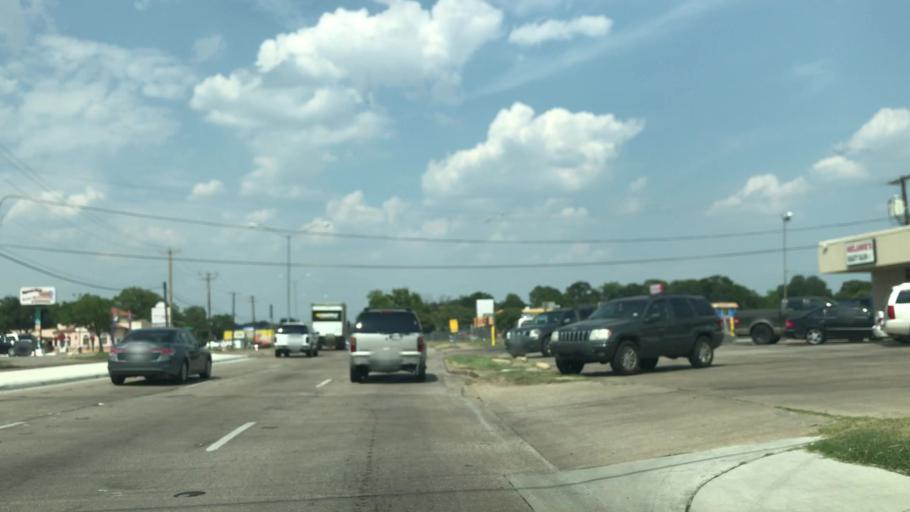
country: US
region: Texas
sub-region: Dallas County
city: University Park
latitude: 32.8565
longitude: -96.8710
